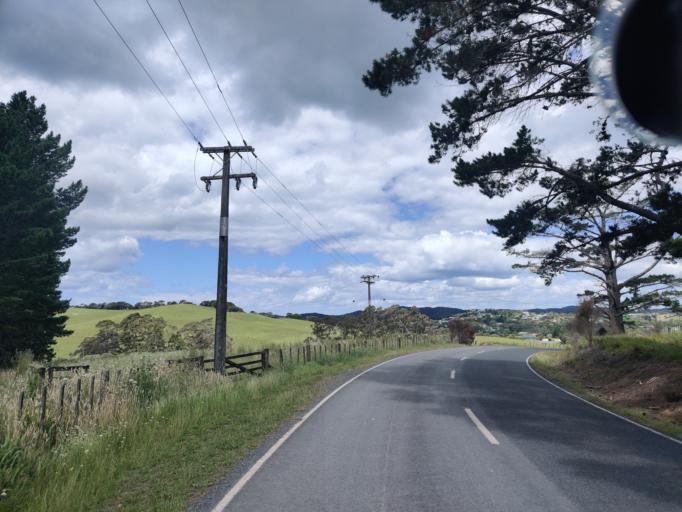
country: NZ
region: Northland
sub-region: Far North District
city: Paihia
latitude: -35.2702
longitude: 174.0476
